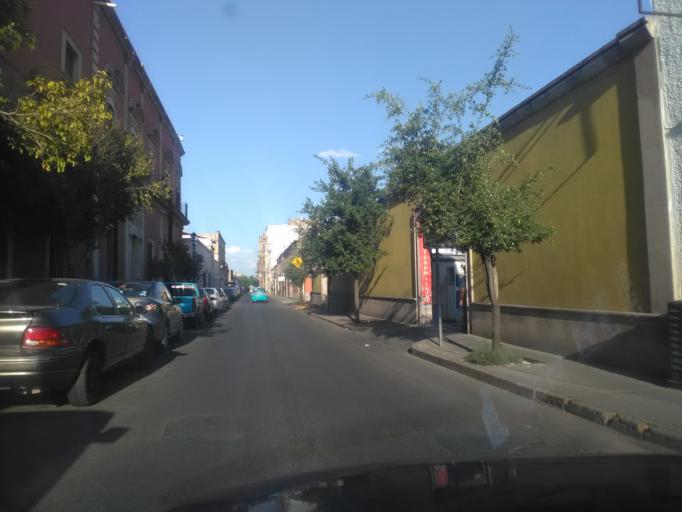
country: MX
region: Durango
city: Victoria de Durango
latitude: 24.0220
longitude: -104.6710
